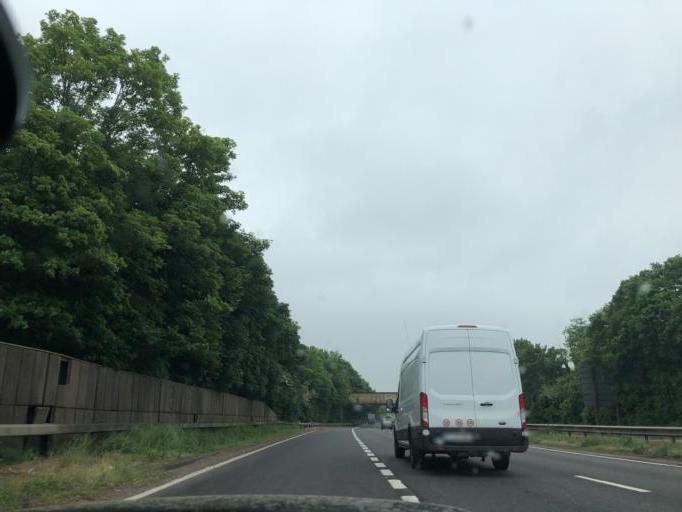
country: GB
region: England
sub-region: Warwickshire
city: Warwick
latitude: 52.2873
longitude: -1.6100
